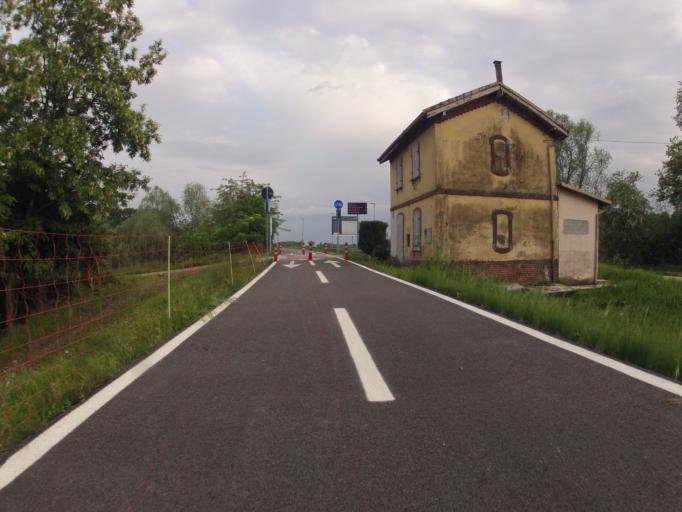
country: IT
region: Piedmont
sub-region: Provincia di Torino
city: Villafranca Piemonte
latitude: 44.7811
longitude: 7.5109
